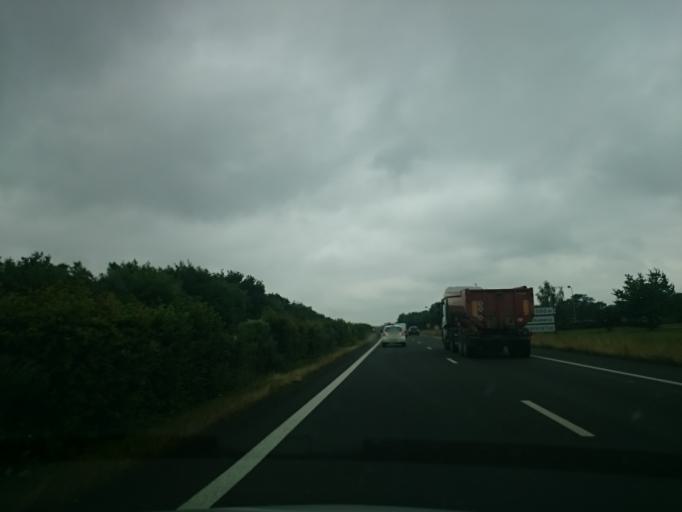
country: FR
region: Pays de la Loire
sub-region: Departement de la Loire-Atlantique
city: Bouguenais
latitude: 47.1672
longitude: -1.6436
